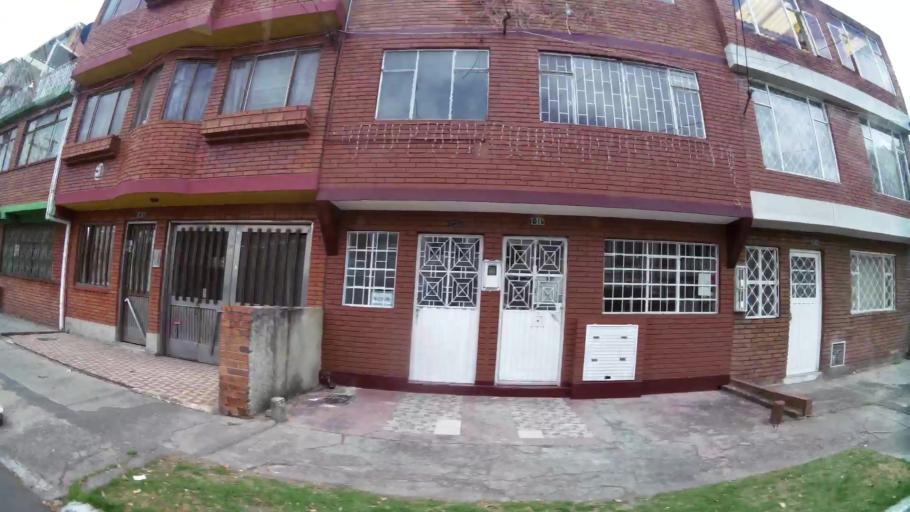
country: CO
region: Bogota D.C.
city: Bogota
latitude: 4.6169
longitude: -74.1236
